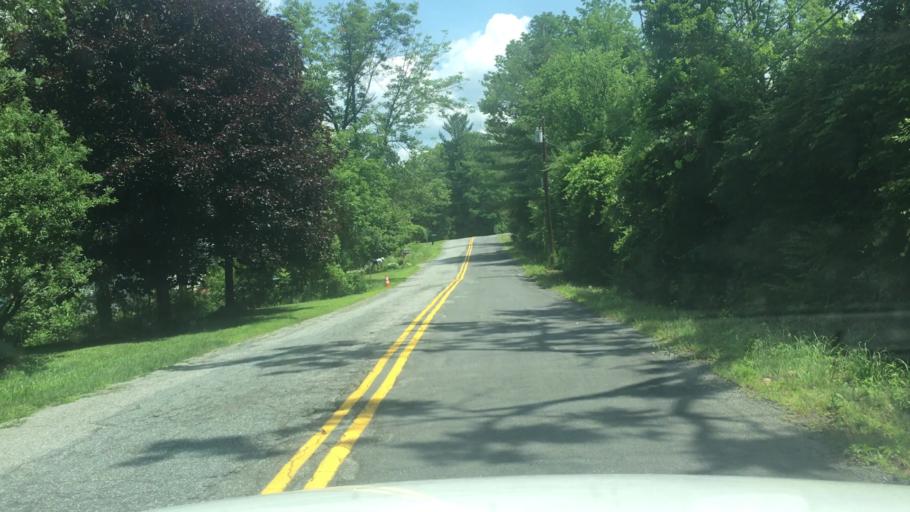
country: US
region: New Hampshire
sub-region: Grafton County
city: Lebanon
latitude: 43.6350
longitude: -72.2237
